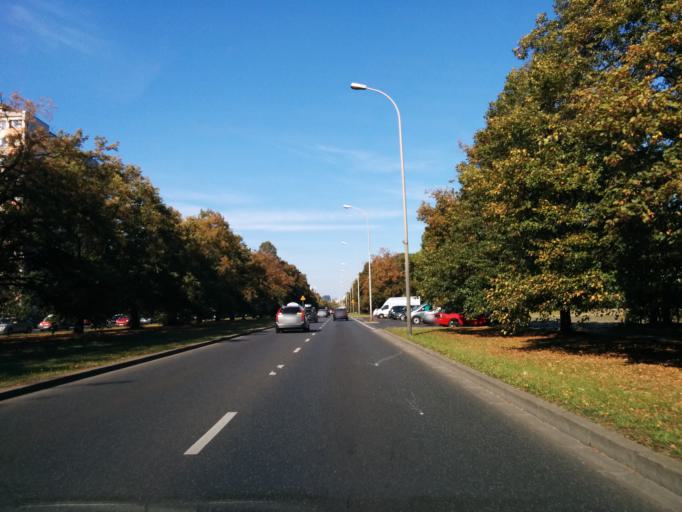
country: PL
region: Masovian Voivodeship
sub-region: Warszawa
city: Ochota
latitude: 52.2024
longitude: 20.9854
